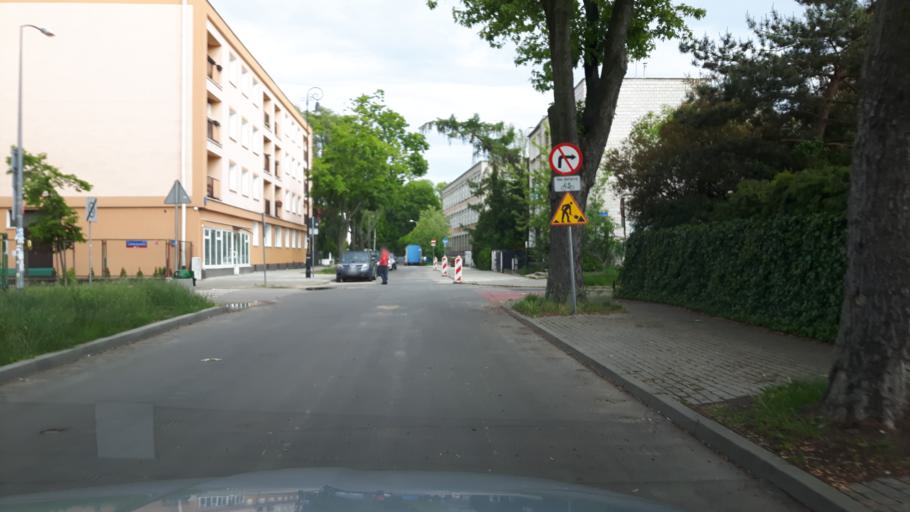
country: PL
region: Masovian Voivodeship
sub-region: Warszawa
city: Praga Poludnie
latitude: 52.2468
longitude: 21.1087
